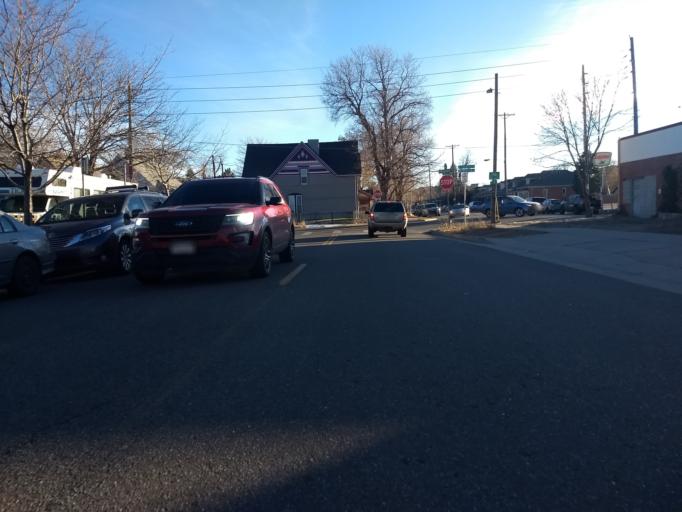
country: US
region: Colorado
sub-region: Denver County
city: Denver
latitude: 39.7152
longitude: -104.9922
